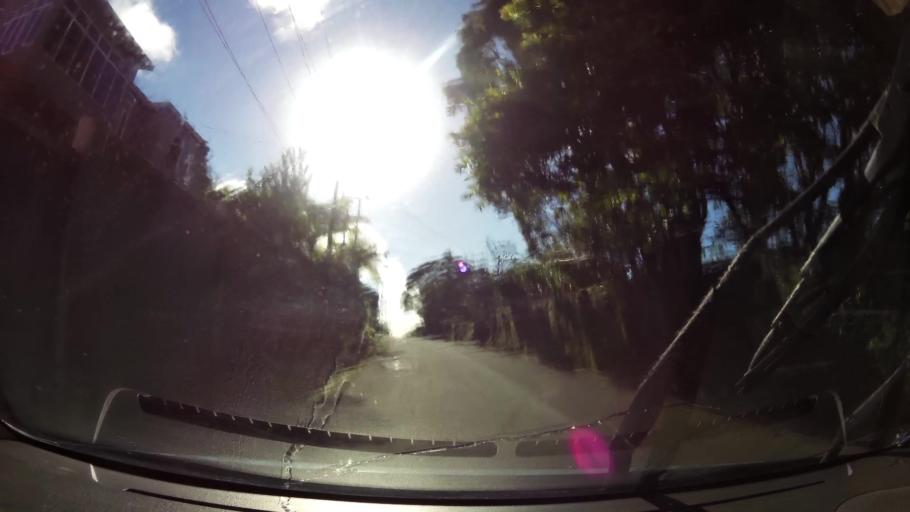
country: MU
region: Plaines Wilhems
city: Curepipe
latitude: -20.3153
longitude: 57.5368
